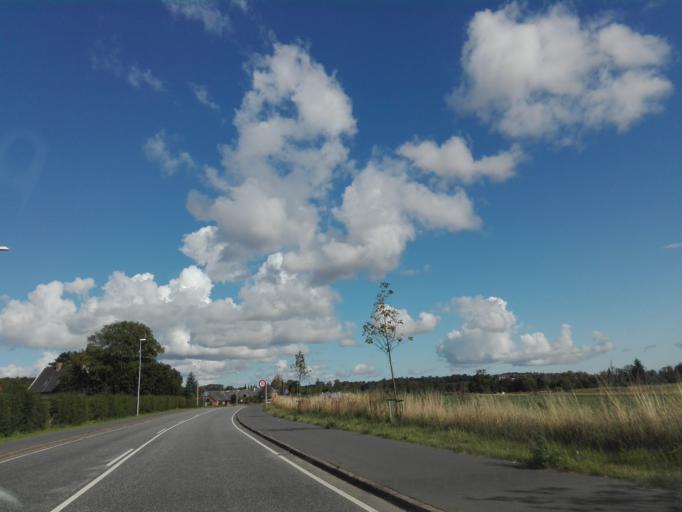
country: DK
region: Central Jutland
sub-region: Randers Kommune
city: Randers
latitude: 56.4593
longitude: 9.9790
